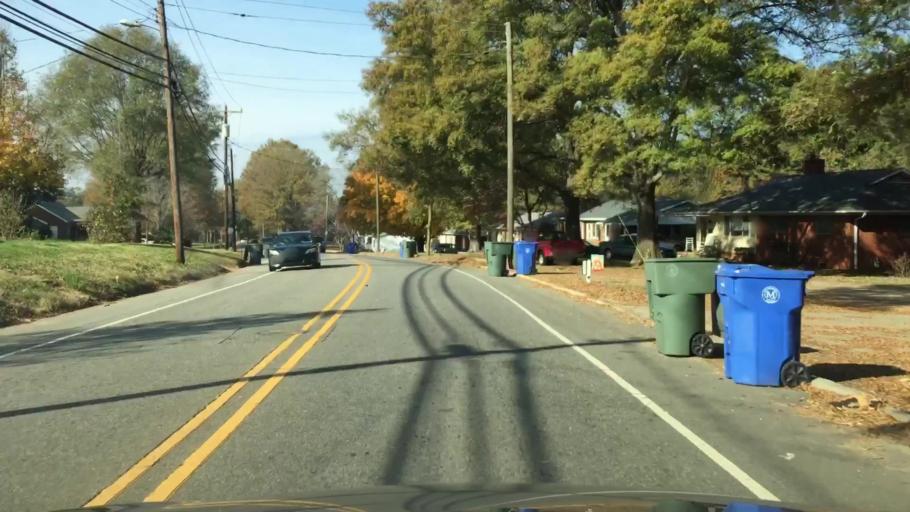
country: US
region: North Carolina
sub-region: Iredell County
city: Mooresville
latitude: 35.5812
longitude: -80.8238
